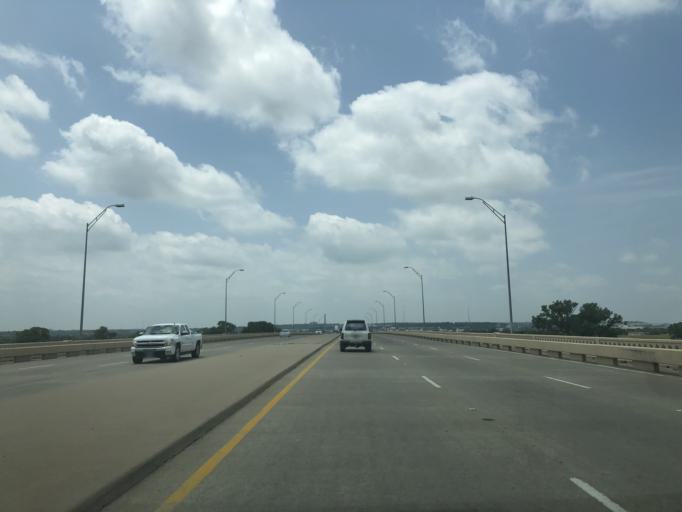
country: US
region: Texas
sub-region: Dallas County
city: Dallas
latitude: 32.7993
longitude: -96.8544
